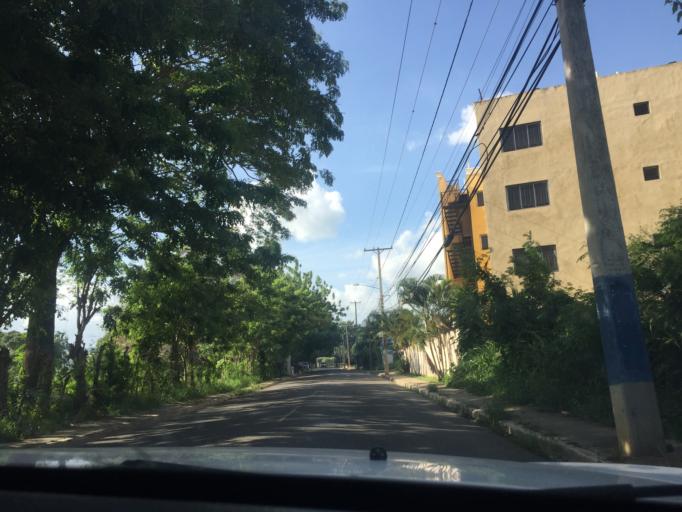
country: DO
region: Santiago
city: Tamboril
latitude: 19.4780
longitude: -70.6558
